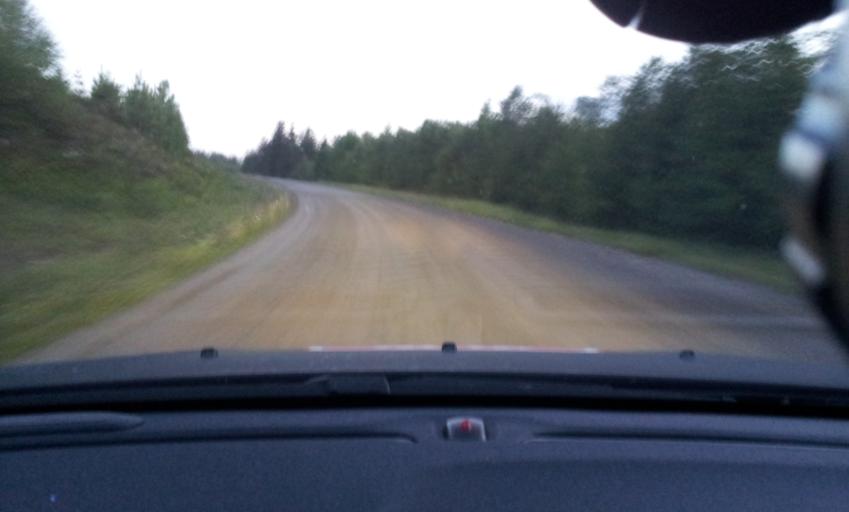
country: SE
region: Vaesternorrland
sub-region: Ange Kommun
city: Ange
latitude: 62.7724
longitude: 15.9196
